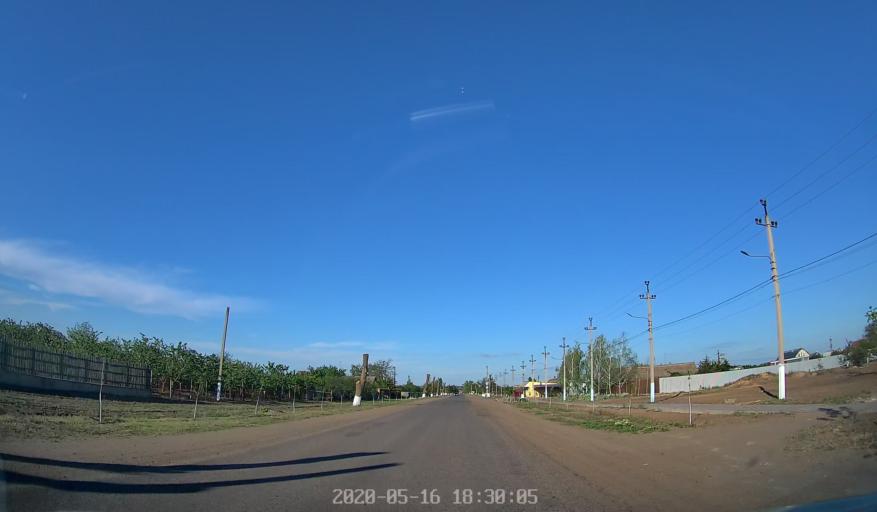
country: UA
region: Odessa
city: Lymanske
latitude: 46.5378
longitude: 30.0264
